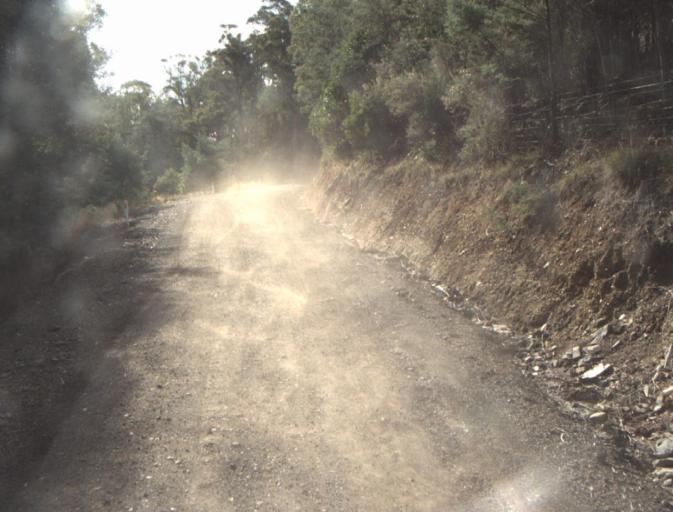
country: AU
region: Tasmania
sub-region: Launceston
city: Mayfield
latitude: -41.2173
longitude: 147.1692
